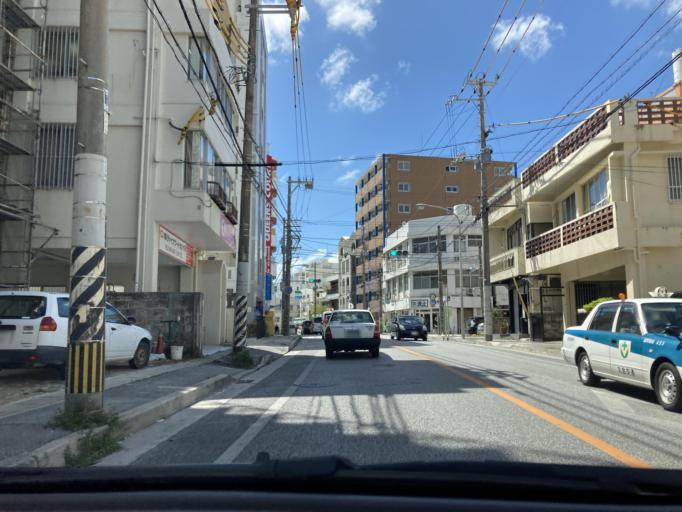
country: JP
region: Okinawa
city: Naha-shi
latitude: 26.2169
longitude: 127.6721
